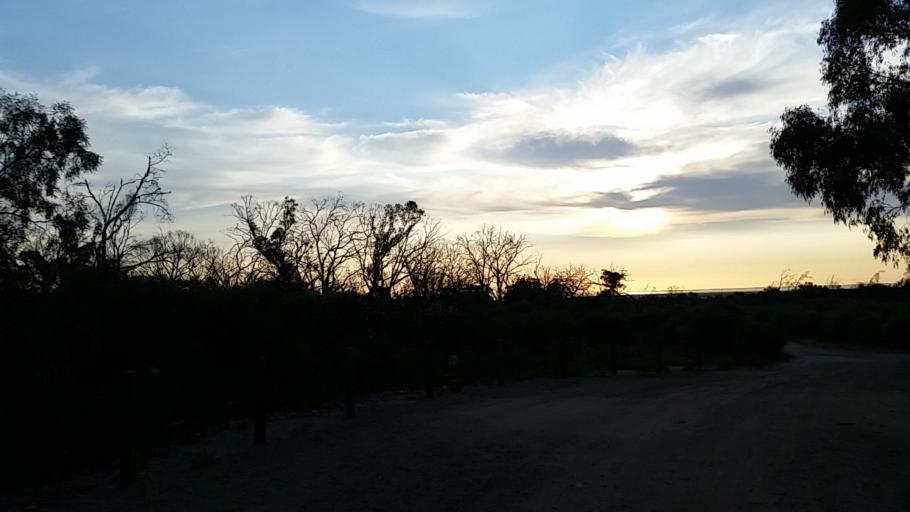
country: AU
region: South Australia
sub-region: Port Pirie City and Dists
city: Port Pirie
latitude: -33.0247
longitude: 138.1029
